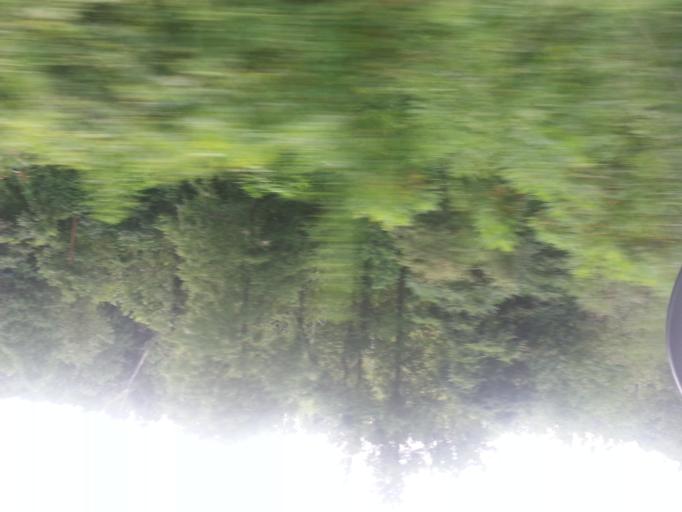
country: US
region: Tennessee
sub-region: Campbell County
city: Caryville
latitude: 36.1982
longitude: -84.3028
